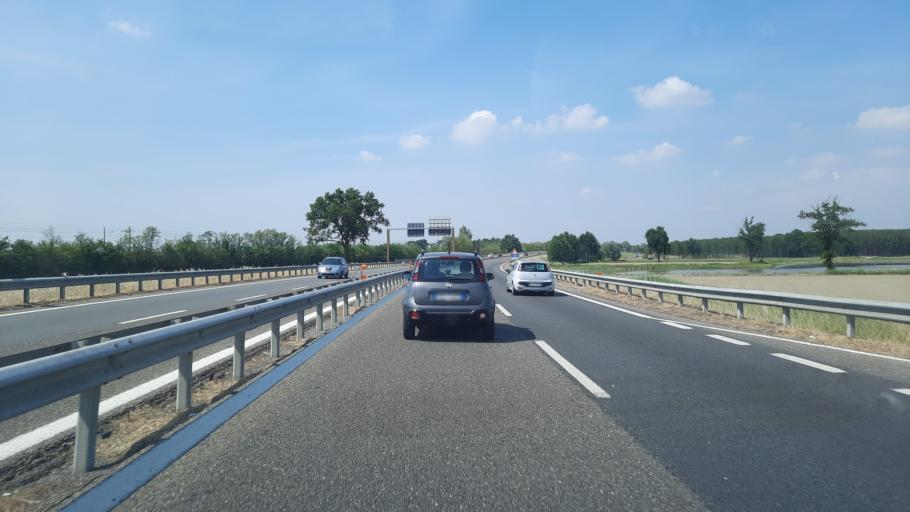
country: IT
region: Lombardy
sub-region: Provincia di Pavia
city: San Martino Siccomario
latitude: 45.1623
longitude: 9.1219
